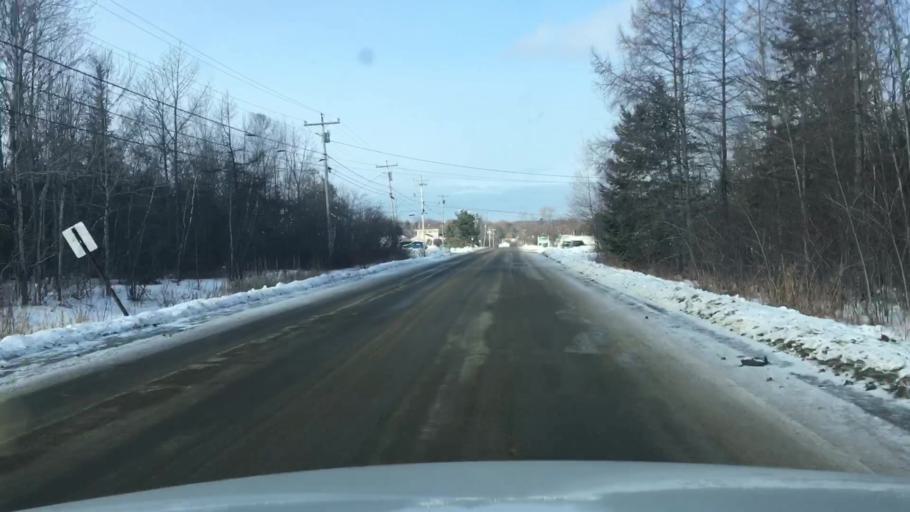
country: US
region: Maine
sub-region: Washington County
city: Calais
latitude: 45.1789
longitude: -67.2654
